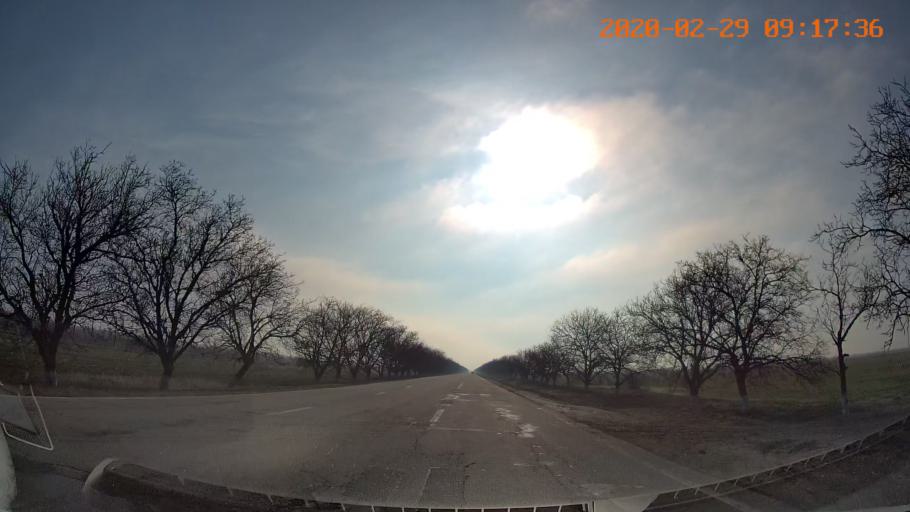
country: MD
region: Telenesti
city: Pervomaisc
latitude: 46.7814
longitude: 29.9073
